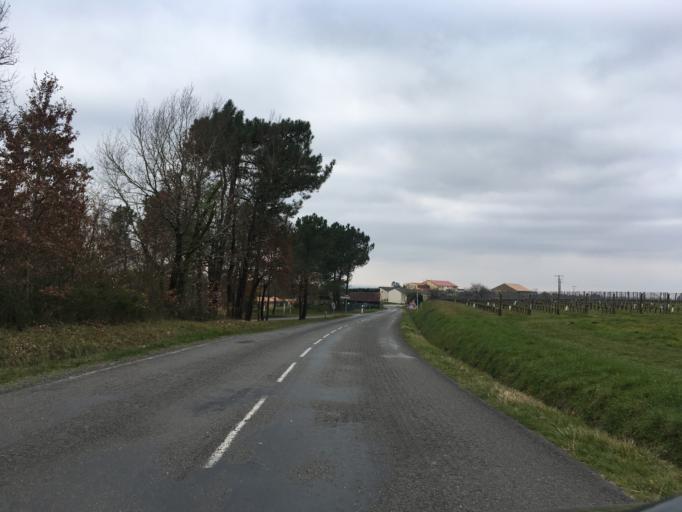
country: FR
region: Aquitaine
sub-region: Departement de la Gironde
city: Saint-Ciers-sur-Gironde
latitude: 45.3159
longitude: -0.5942
